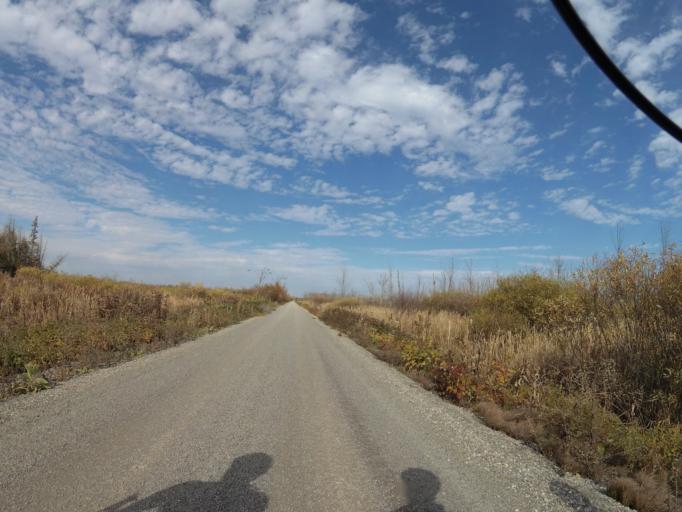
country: CA
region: Ontario
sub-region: Lanark County
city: Smiths Falls
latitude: 45.0176
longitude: -76.0737
